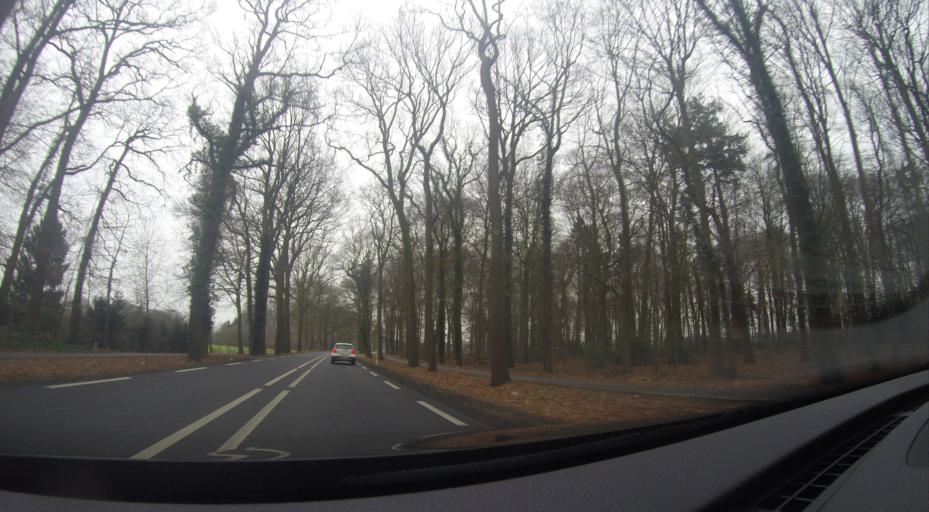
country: NL
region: Gelderland
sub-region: Gemeente Lochem
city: Almen
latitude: 52.1235
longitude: 6.2831
